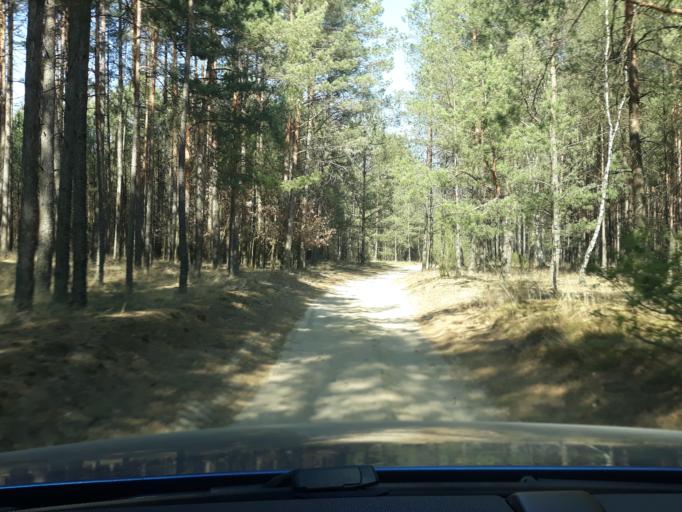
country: PL
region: Pomeranian Voivodeship
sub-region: Powiat bytowski
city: Lipnica
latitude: 53.8543
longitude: 17.4329
